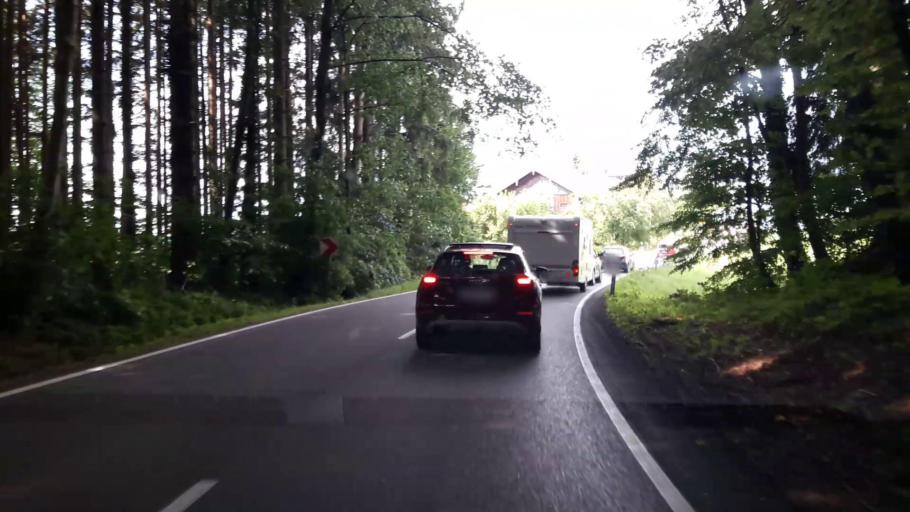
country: DE
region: Bavaria
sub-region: Upper Bavaria
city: Anger
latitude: 47.8245
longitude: 12.8395
